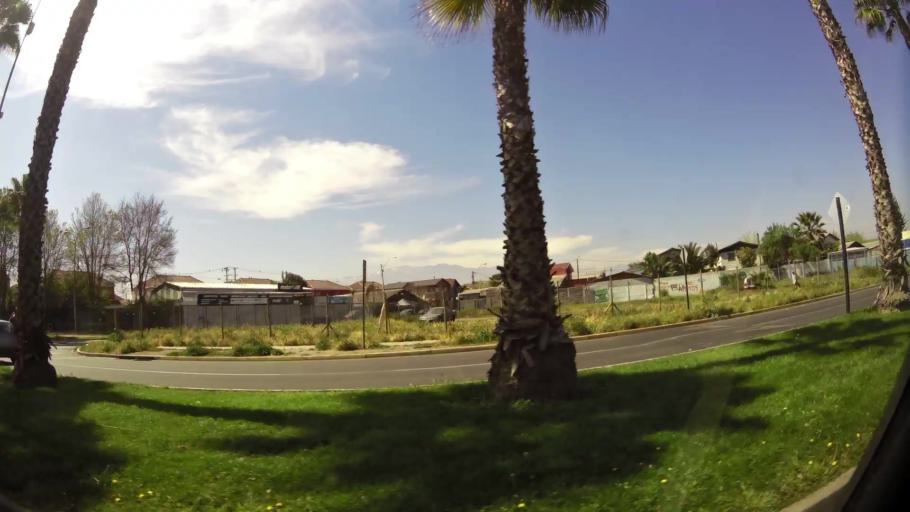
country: CL
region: Santiago Metropolitan
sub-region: Provincia de Santiago
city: Lo Prado
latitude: -33.4889
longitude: -70.7425
